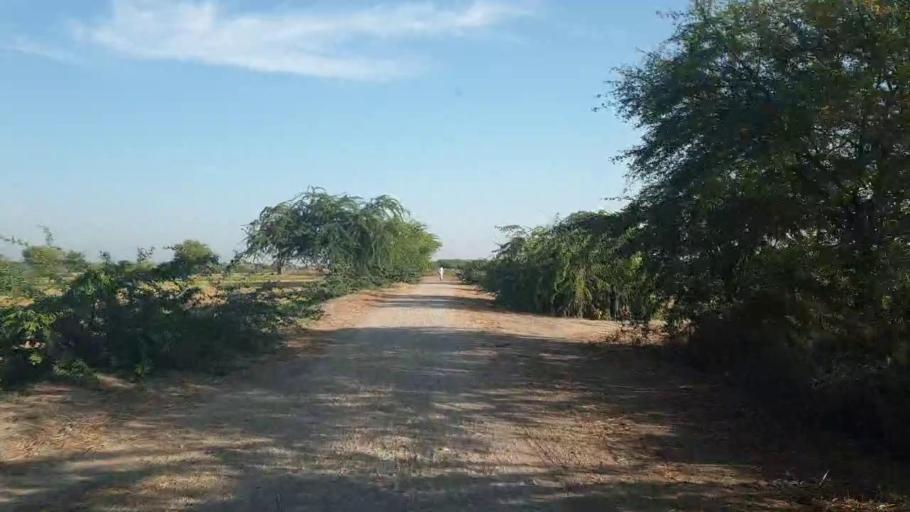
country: PK
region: Sindh
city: Talhar
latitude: 24.8111
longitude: 68.8391
